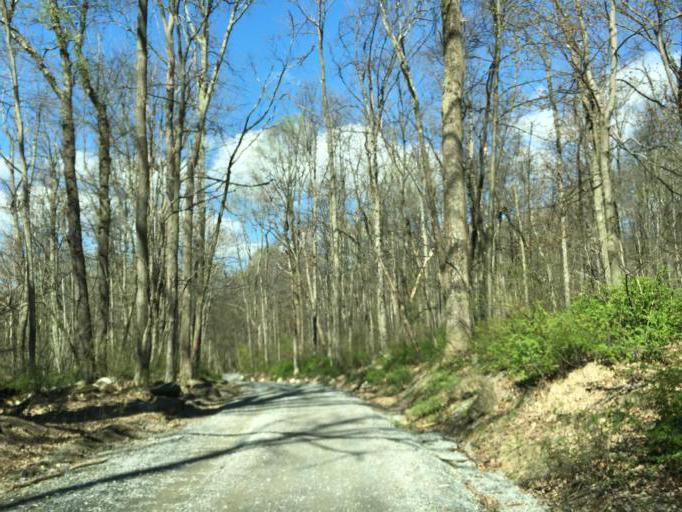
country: US
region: Maryland
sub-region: Washington County
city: Highfield-Cascade
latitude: 39.6515
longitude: -77.4788
